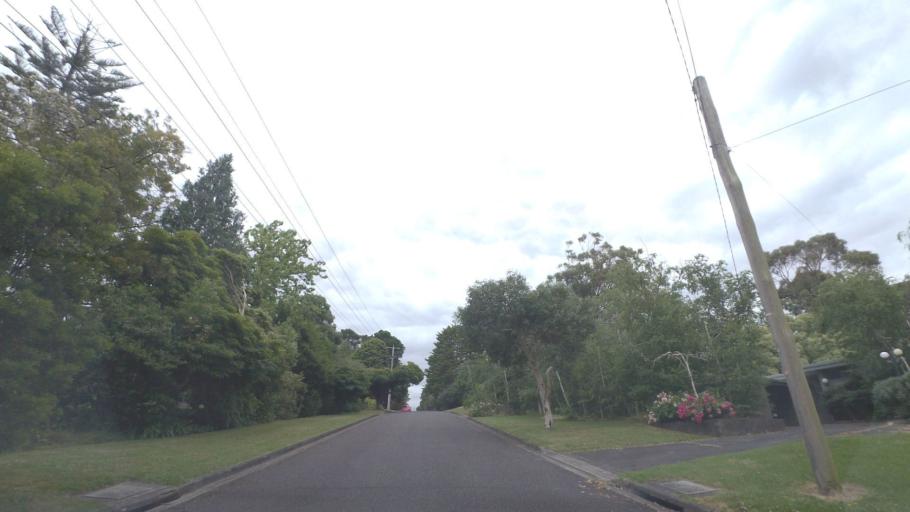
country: AU
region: Victoria
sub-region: Manningham
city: Park Orchards
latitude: -37.7824
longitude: 145.2229
